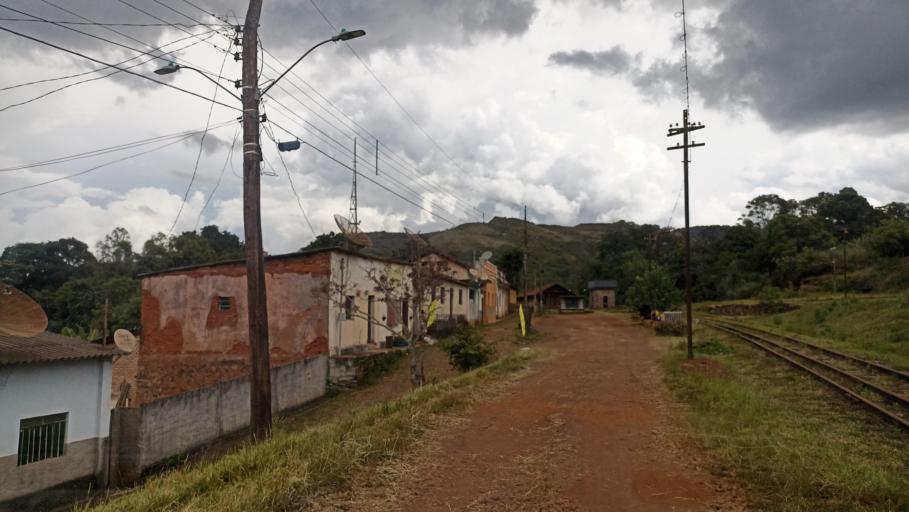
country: BR
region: Minas Gerais
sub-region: Congonhas
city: Congonhas
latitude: -20.4346
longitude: -43.7723
